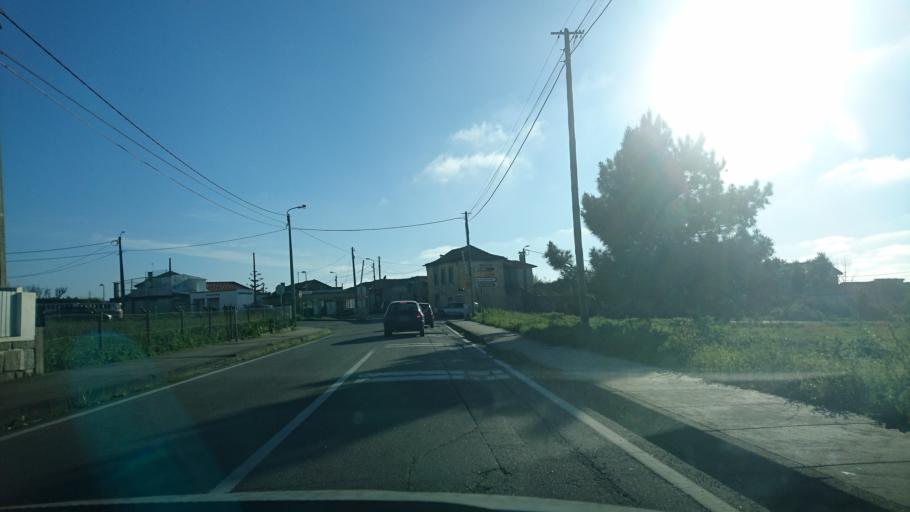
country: PT
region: Aveiro
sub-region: Espinho
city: Silvalde
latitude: 40.9895
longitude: -8.6302
